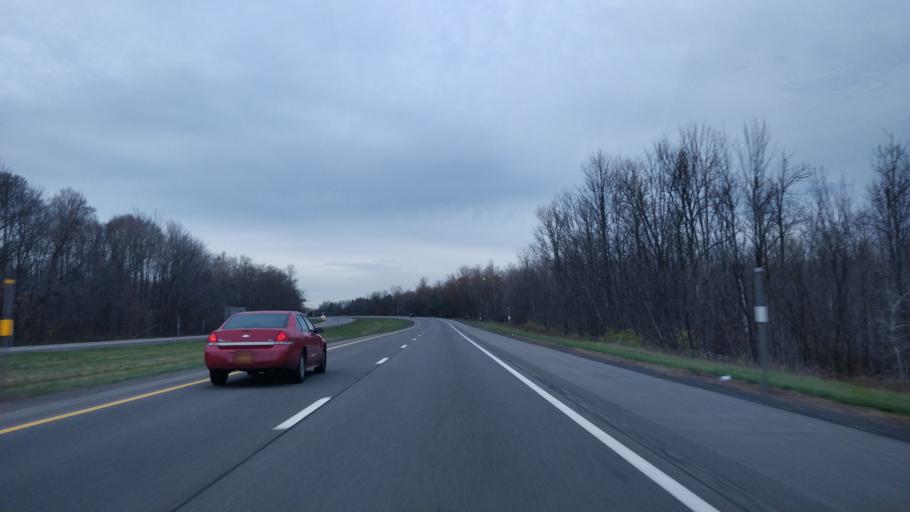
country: US
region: New York
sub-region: Oswego County
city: Central Square
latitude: 43.2966
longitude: -76.1245
